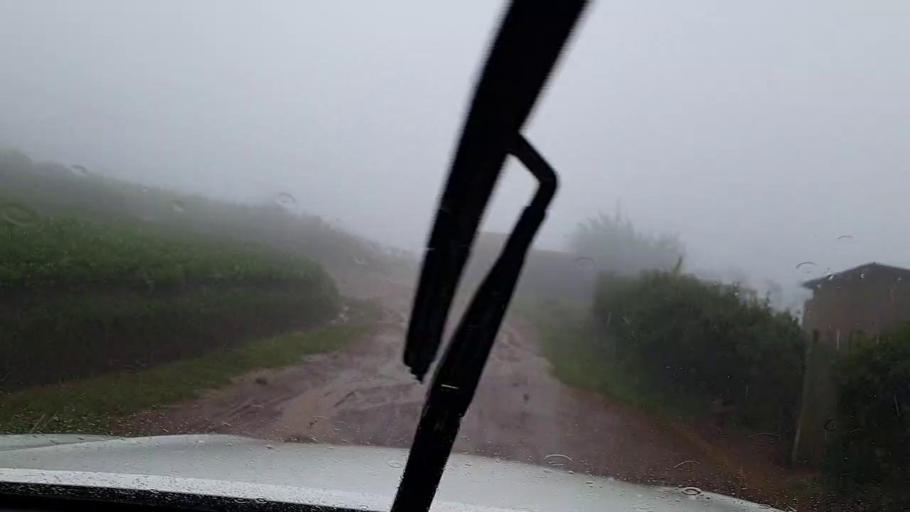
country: RW
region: Northern Province
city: Byumba
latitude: -1.7309
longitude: 30.0161
